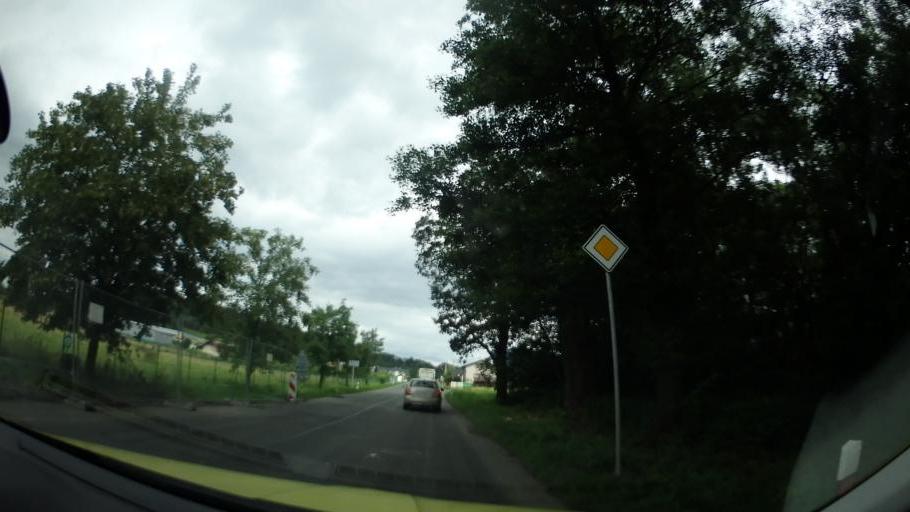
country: CZ
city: Verovice
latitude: 49.5413
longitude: 18.0927
